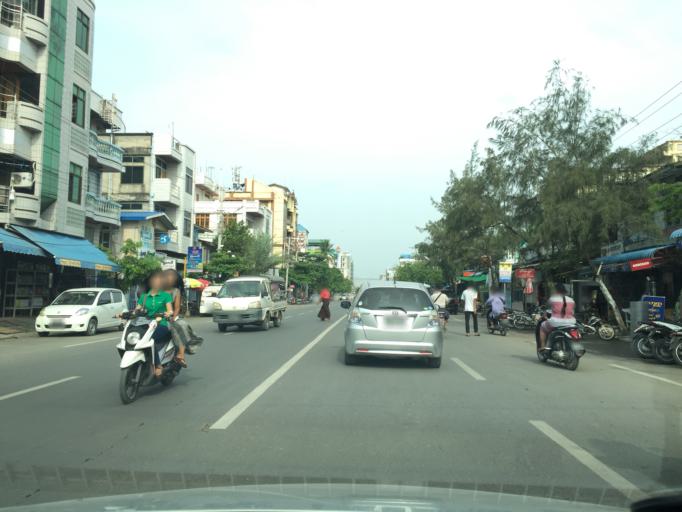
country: MM
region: Mandalay
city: Mandalay
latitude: 21.9688
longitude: 96.0913
